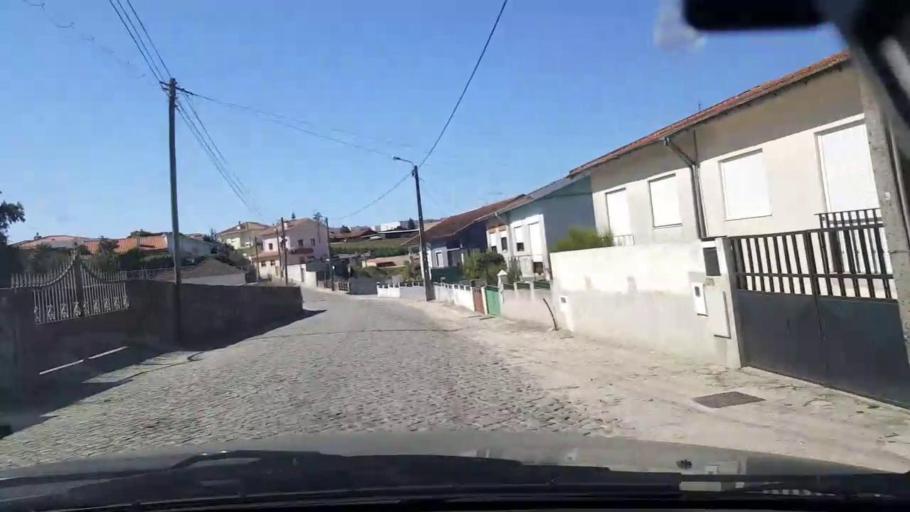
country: PT
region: Porto
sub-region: Matosinhos
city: Lavra
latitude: 41.2962
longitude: -8.6864
